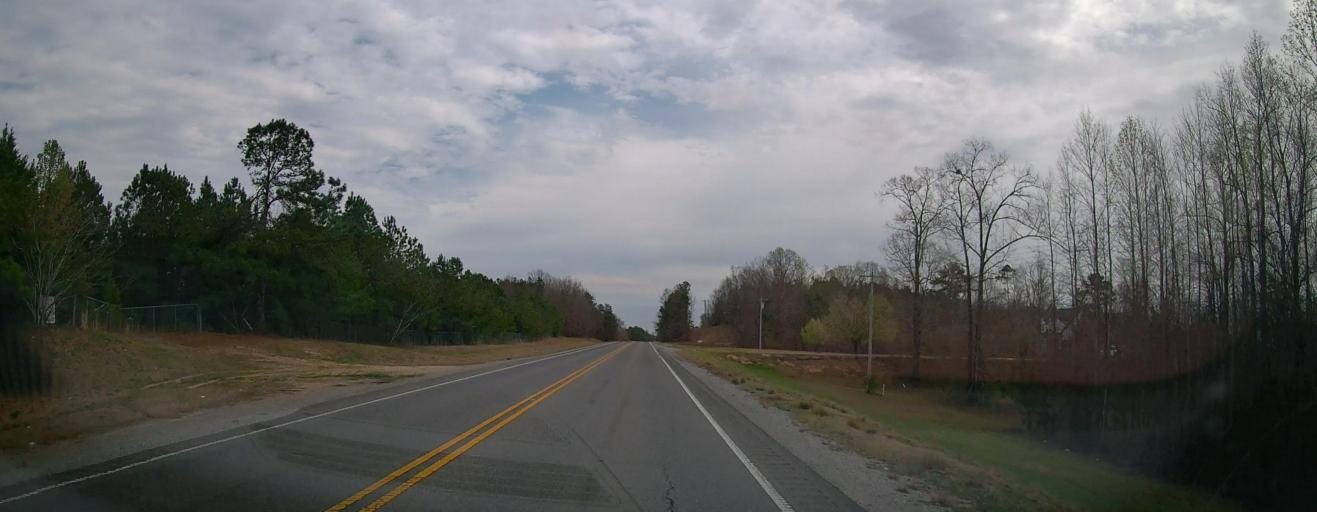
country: US
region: Alabama
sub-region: Marion County
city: Guin
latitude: 34.0345
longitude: -87.9473
